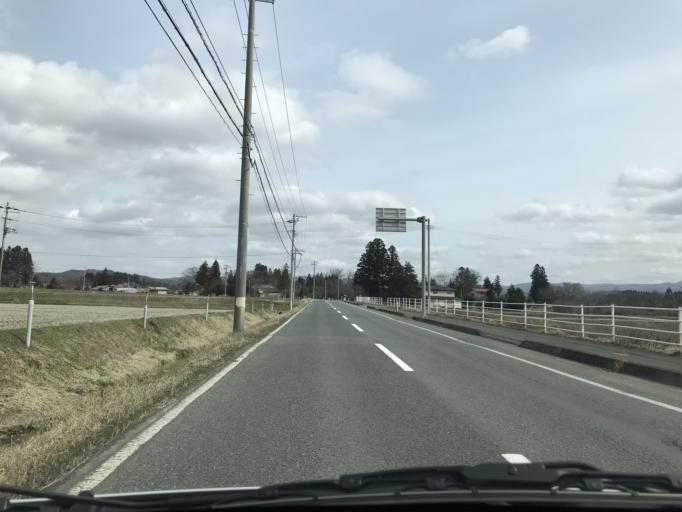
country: JP
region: Iwate
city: Kitakami
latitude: 39.2211
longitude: 141.2258
